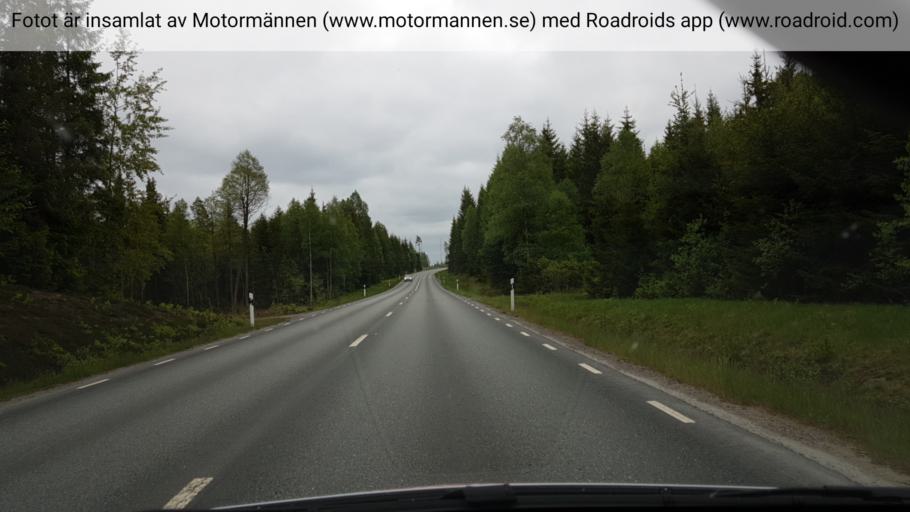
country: SE
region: Joenkoeping
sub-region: Savsjo Kommun
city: Saevsjoe
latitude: 57.3932
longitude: 14.7104
